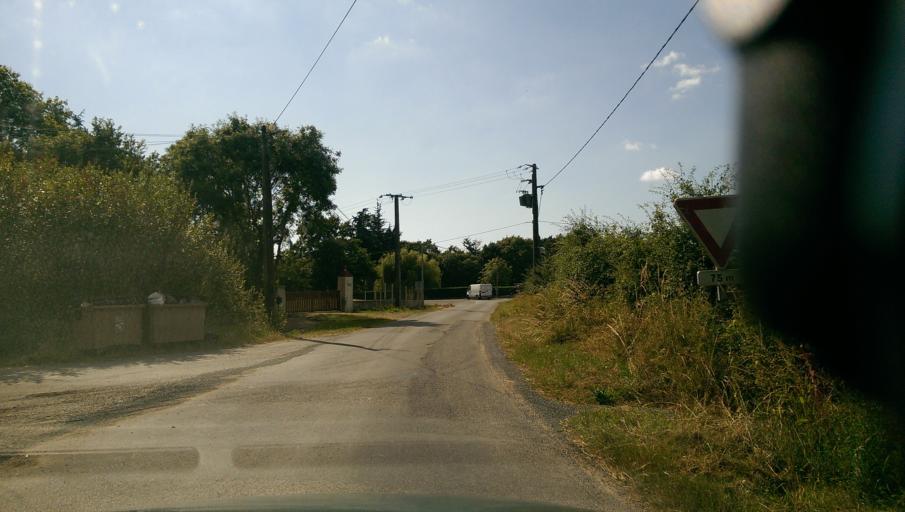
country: FR
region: Pays de la Loire
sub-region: Departement de la Loire-Atlantique
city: Lege
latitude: 46.9007
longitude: -1.5688
